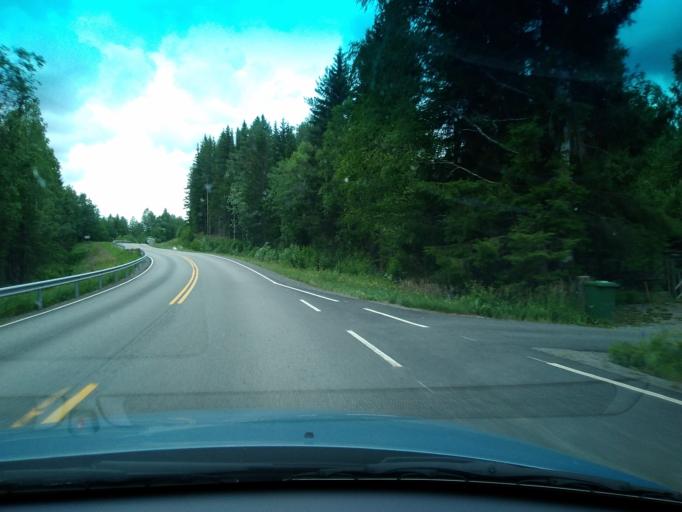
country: FI
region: Central Finland
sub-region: Saarijaervi-Viitasaari
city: Pylkoenmaeki
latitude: 62.6493
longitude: 25.0073
